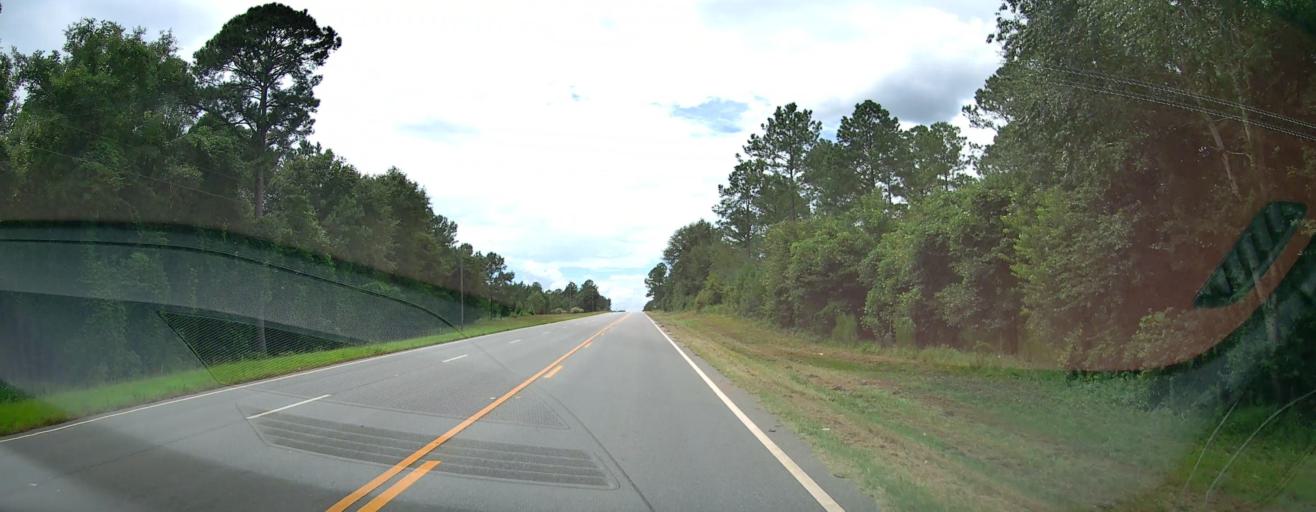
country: US
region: Georgia
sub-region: Macon County
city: Oglethorpe
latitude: 32.2823
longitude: -84.1490
